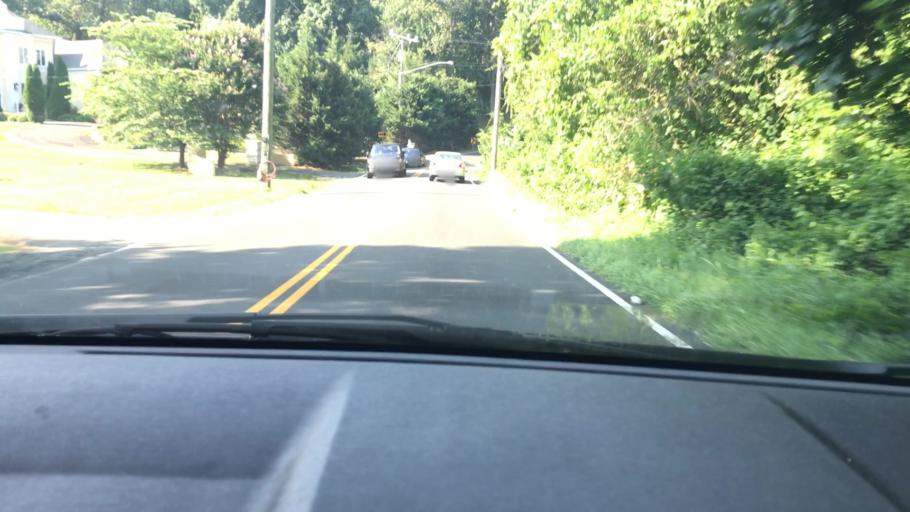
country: US
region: Virginia
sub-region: Fairfax County
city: Tysons Corner
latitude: 38.9452
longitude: -77.2294
